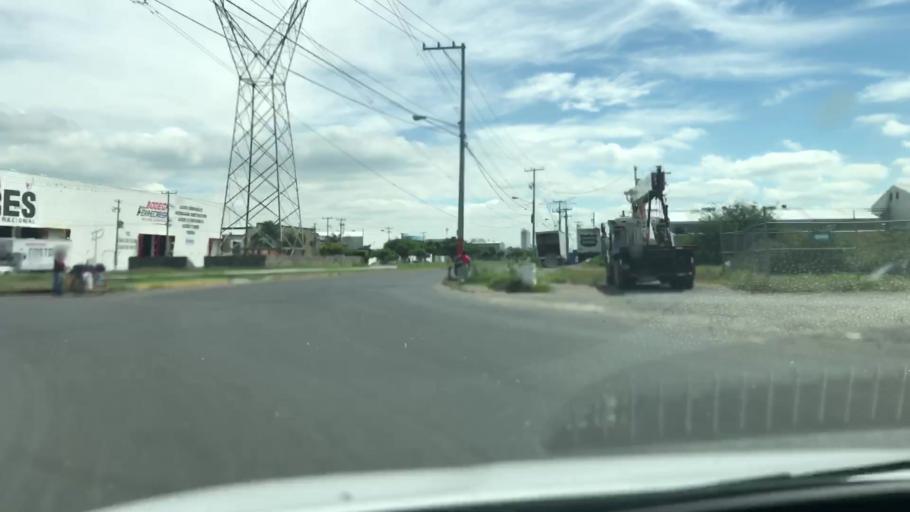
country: MX
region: Guanajuato
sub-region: Celaya
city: La Trinidad
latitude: 20.5504
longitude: -100.8032
